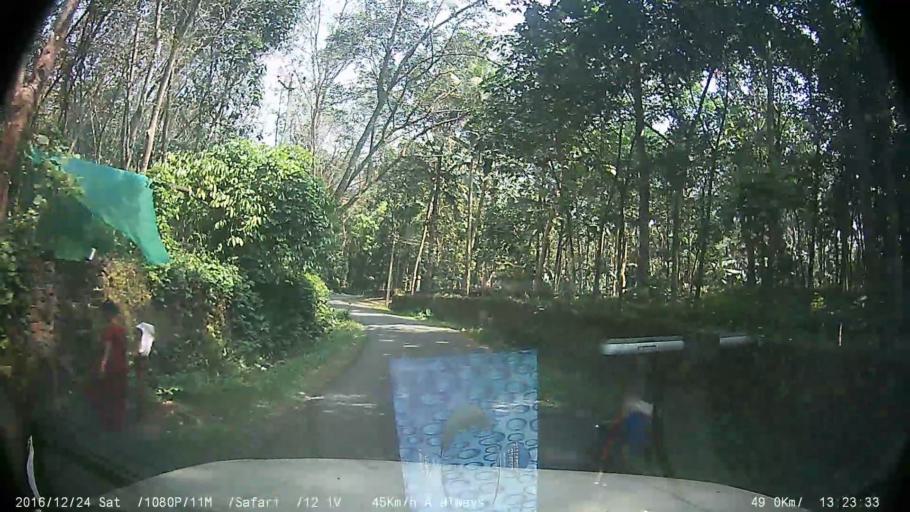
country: IN
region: Kerala
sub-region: Kottayam
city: Palackattumala
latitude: 9.8700
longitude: 76.6717
